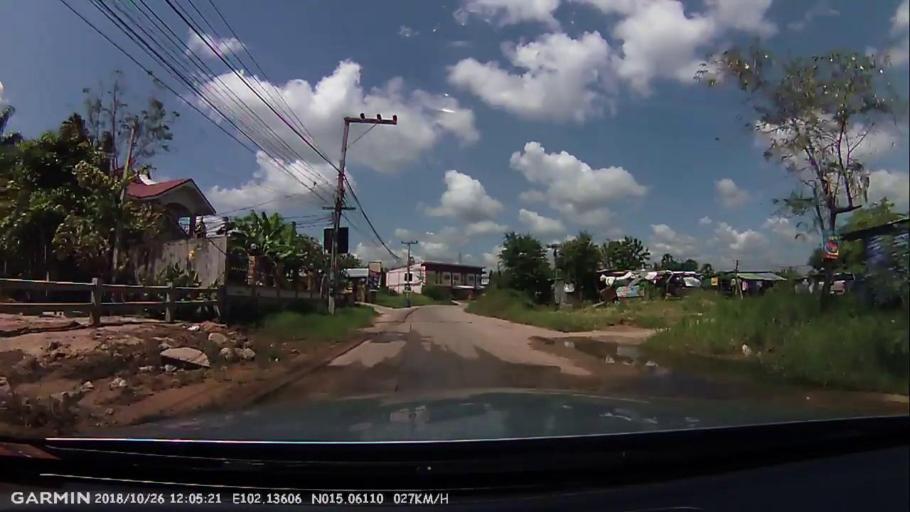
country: TH
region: Nakhon Ratchasima
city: Nakhon Ratchasima
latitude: 15.0610
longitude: 102.1361
